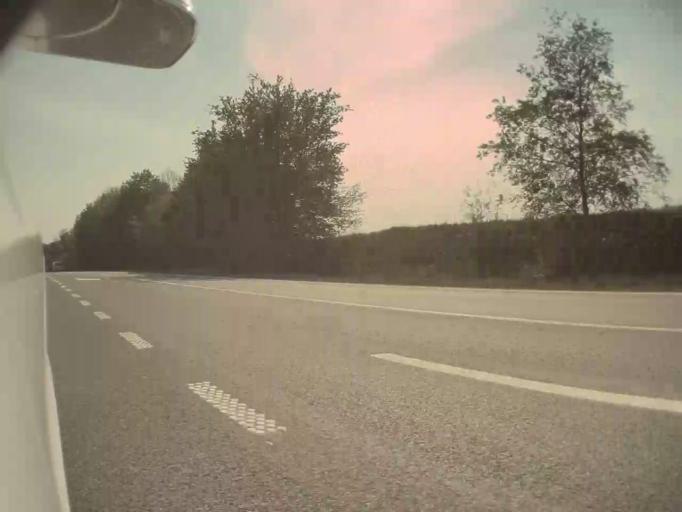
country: BE
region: Wallonia
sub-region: Province de Namur
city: Ciney
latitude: 50.3109
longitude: 5.1238
